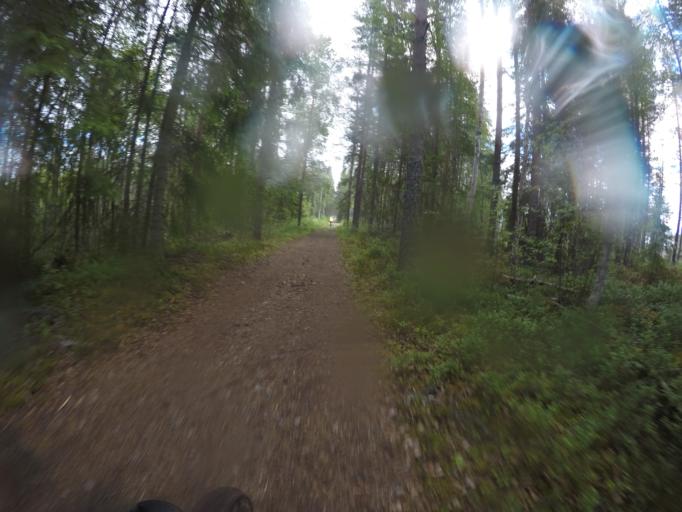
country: SE
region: Vaermland
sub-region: Filipstads Kommun
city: Lesjofors
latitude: 60.1394
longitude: 14.2610
